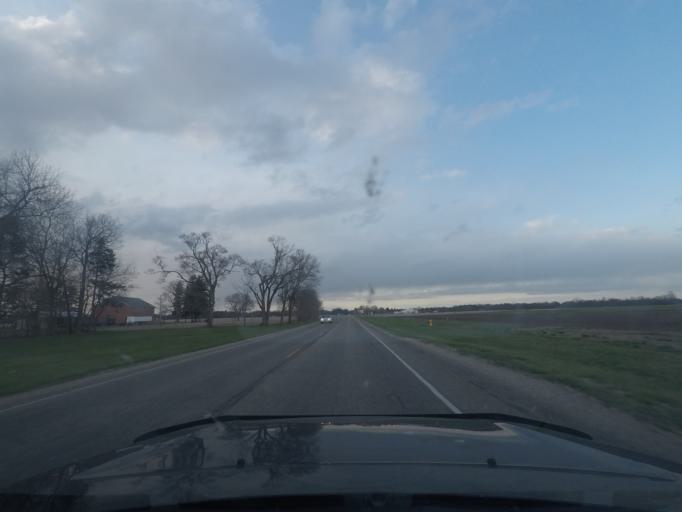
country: US
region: Indiana
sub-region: LaPorte County
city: LaPorte
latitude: 41.5743
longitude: -86.7394
